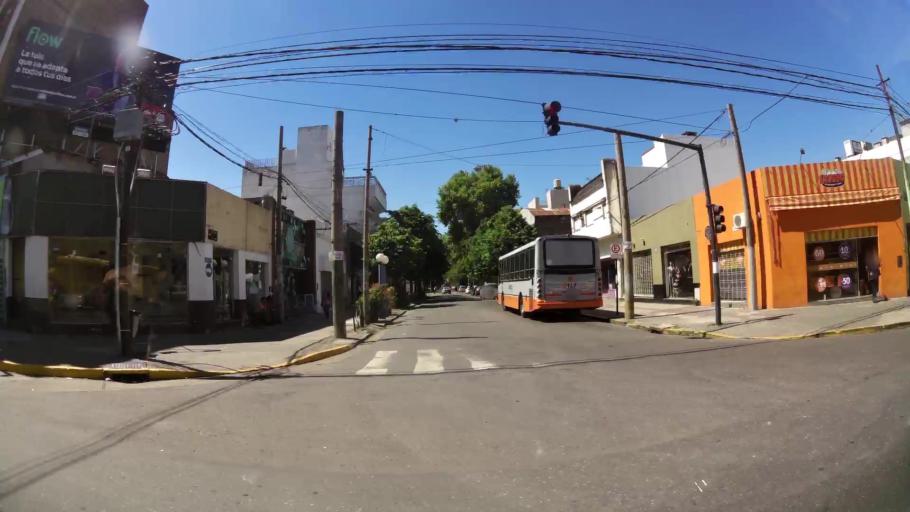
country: AR
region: Santa Fe
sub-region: Departamento de Rosario
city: Rosario
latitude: -32.9390
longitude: -60.6720
